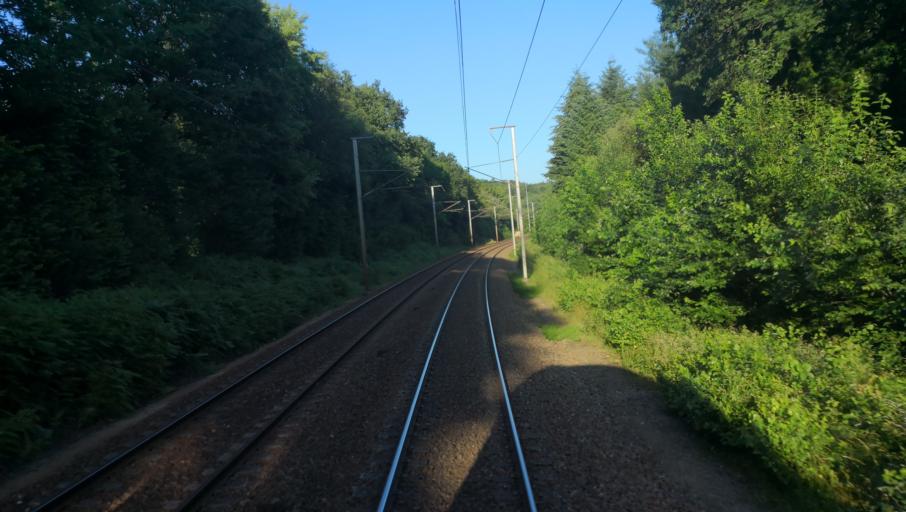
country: FR
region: Haute-Normandie
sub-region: Departement de l'Eure
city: Bernay
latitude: 49.0948
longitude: 0.5526
